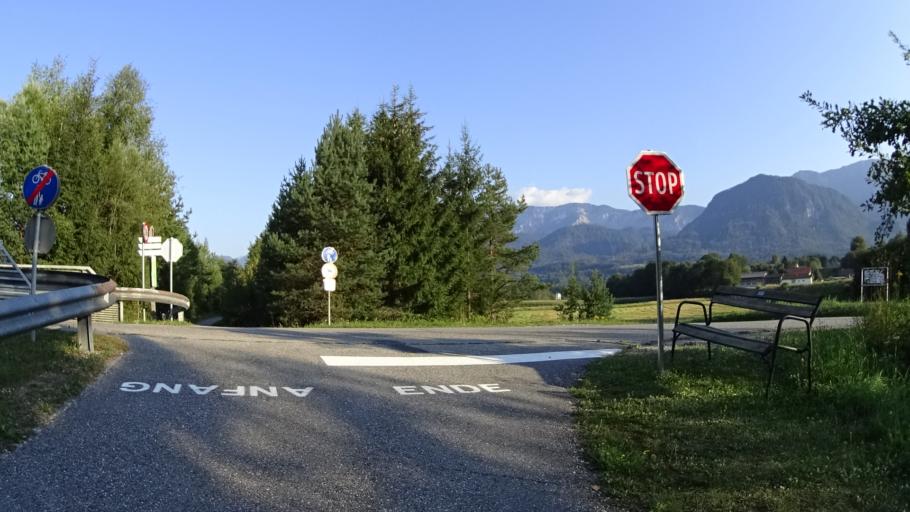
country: AT
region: Carinthia
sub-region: Politischer Bezirk Villach Land
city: Sankt Jakob
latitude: 46.5469
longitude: 14.0867
